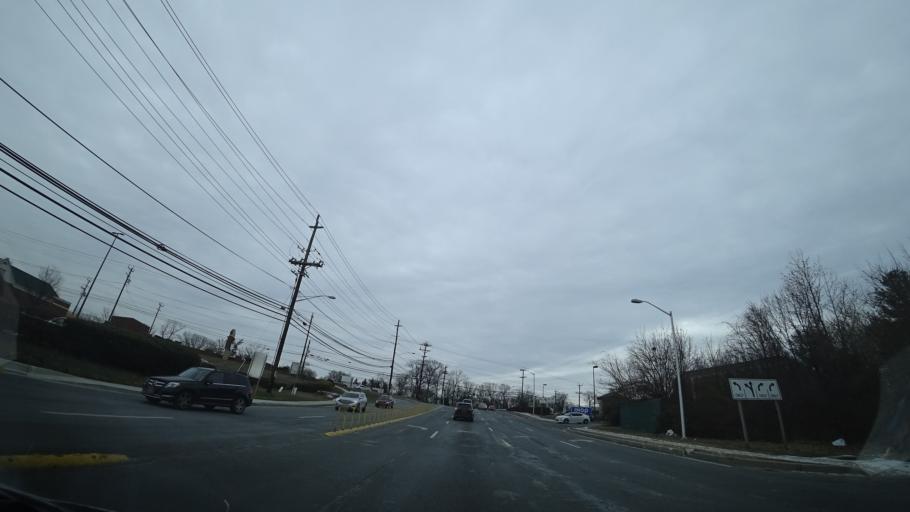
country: US
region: Maryland
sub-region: Prince George's County
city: Berwyn Heights
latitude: 39.0151
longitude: -76.9290
